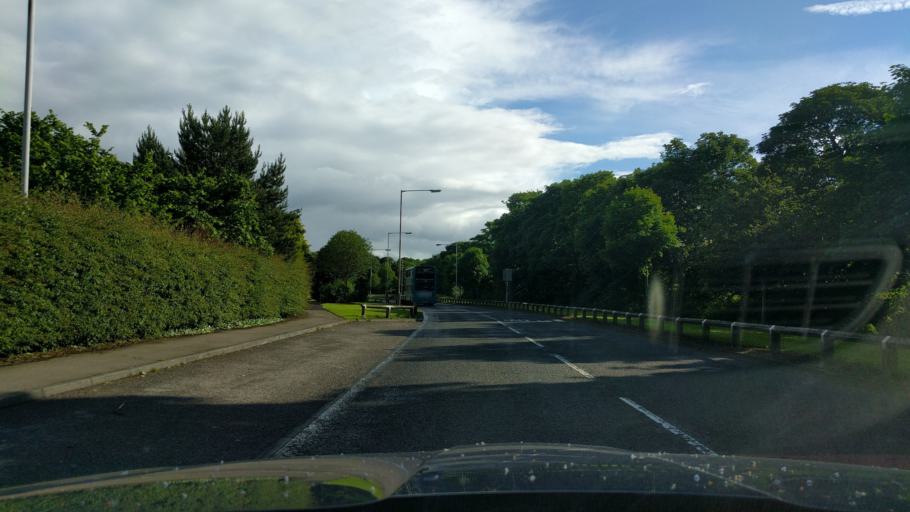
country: GB
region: England
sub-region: Northumberland
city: Cramlington
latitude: 55.0979
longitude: -1.5896
